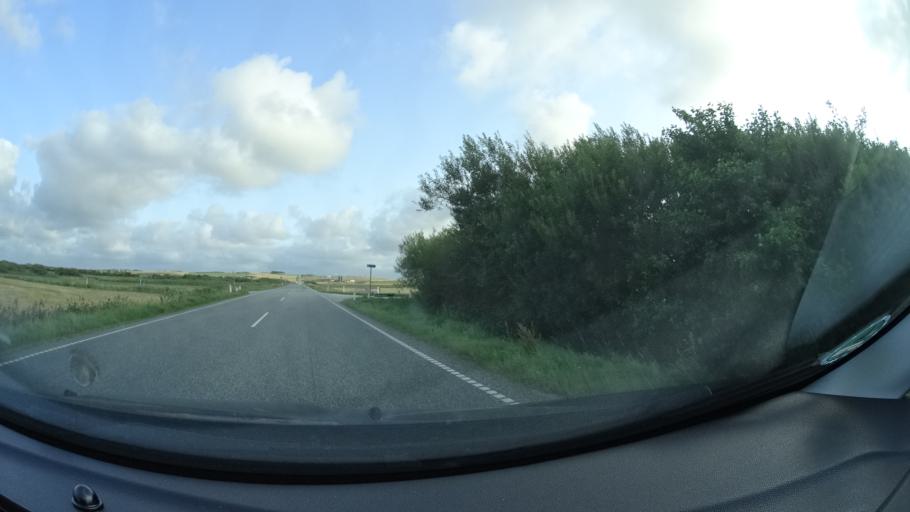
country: DK
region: Central Jutland
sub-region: Lemvig Kommune
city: Harboore
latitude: 56.6030
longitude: 8.1837
